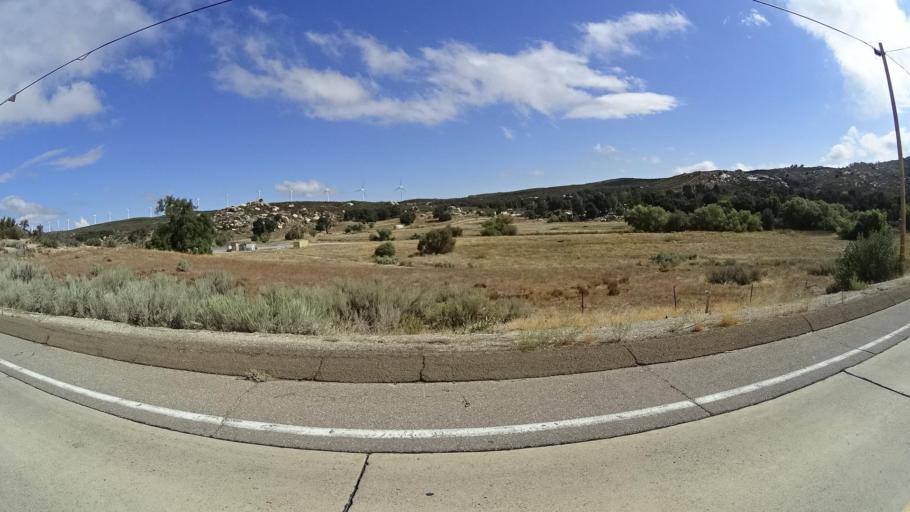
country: US
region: California
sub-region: San Diego County
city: Campo
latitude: 32.6903
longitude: -116.3398
